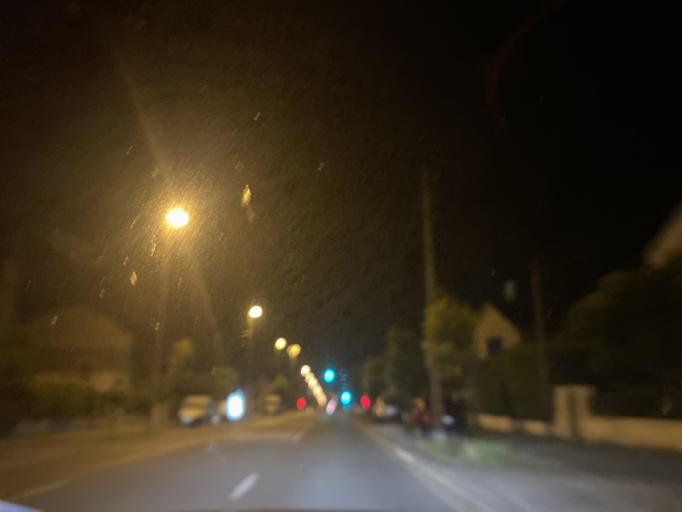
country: FR
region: Centre
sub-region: Departement du Cher
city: Bourges
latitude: 47.0700
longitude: 2.3801
